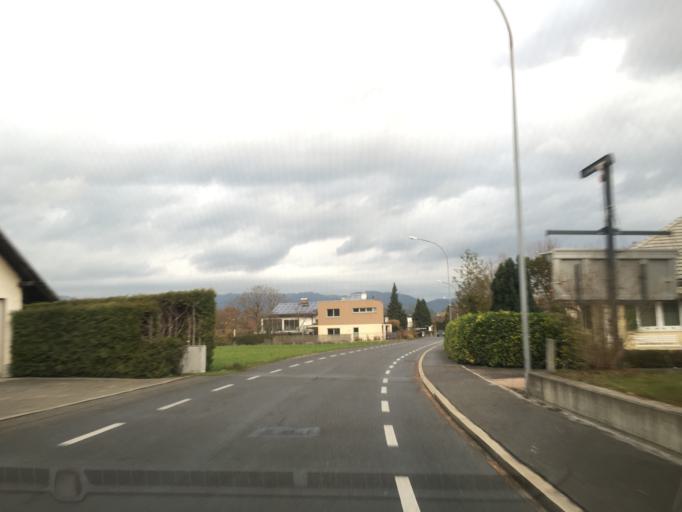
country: AT
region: Vorarlberg
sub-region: Politischer Bezirk Feldkirch
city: Gotzis
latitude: 47.3380
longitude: 9.6261
